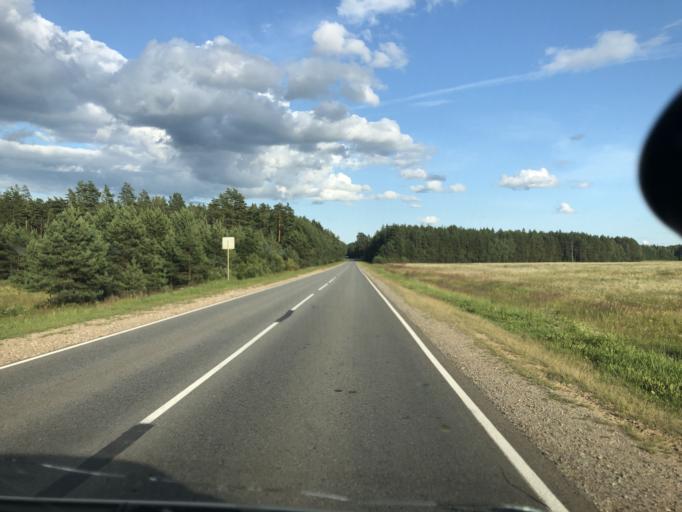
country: RU
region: Kaluga
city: Yukhnov
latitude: 54.7174
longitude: 35.2307
